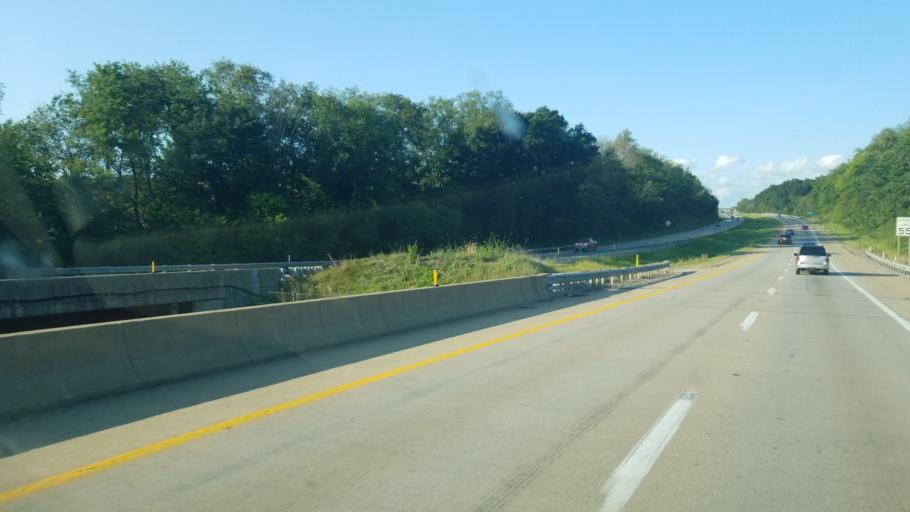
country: US
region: Pennsylvania
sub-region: Washington County
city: Cecil-Bishop
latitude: 40.3048
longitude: -80.1613
